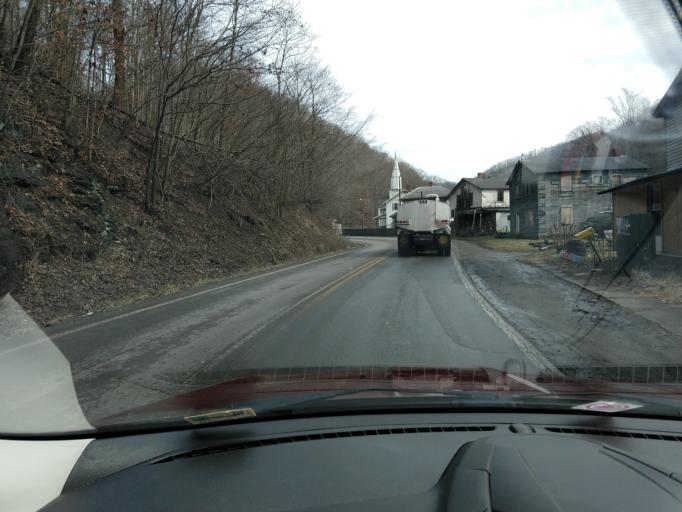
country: US
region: West Virginia
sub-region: McDowell County
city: Welch
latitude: 37.3342
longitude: -81.6760
